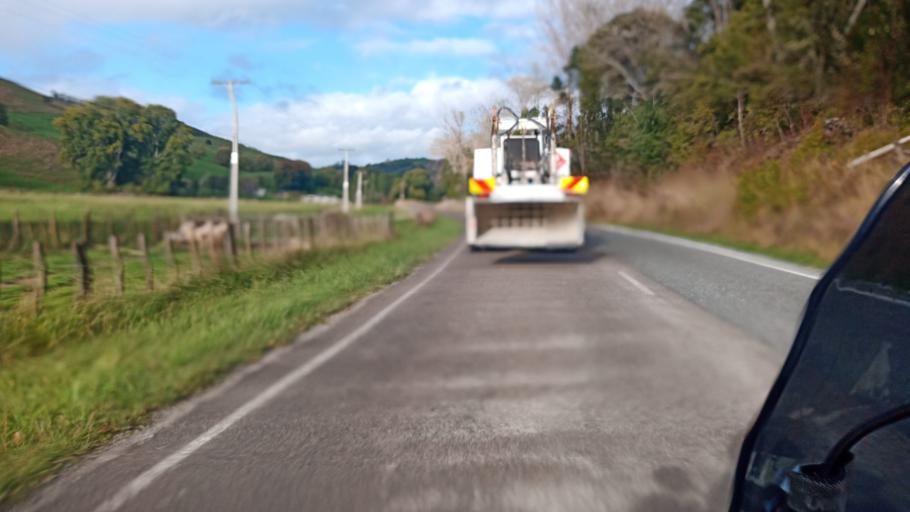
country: NZ
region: Gisborne
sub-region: Gisborne District
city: Gisborne
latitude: -38.5880
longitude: 177.7843
